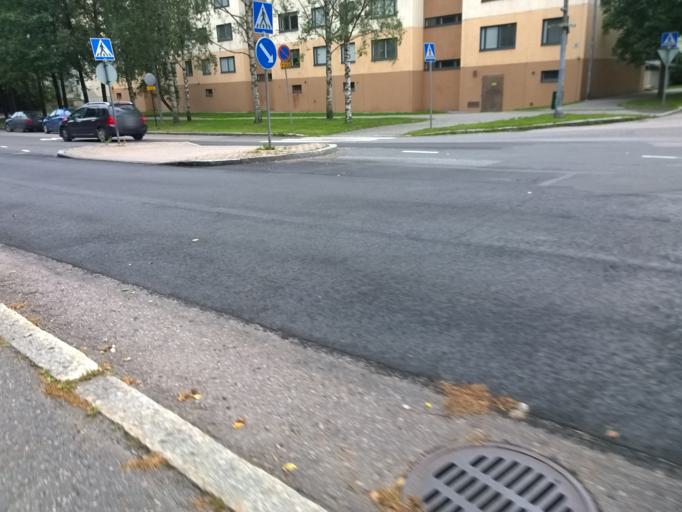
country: FI
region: Pirkanmaa
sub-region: Tampere
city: Tampere
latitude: 61.4466
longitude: 23.8471
